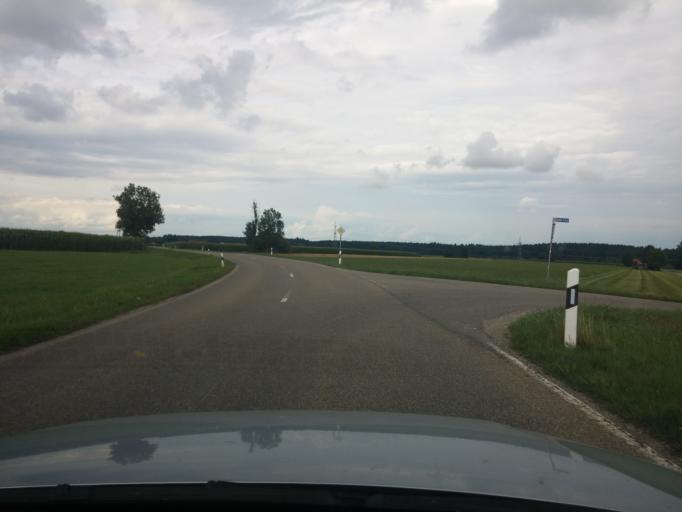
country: DE
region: Bavaria
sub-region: Swabia
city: Kronburg
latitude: 47.9398
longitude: 10.1617
